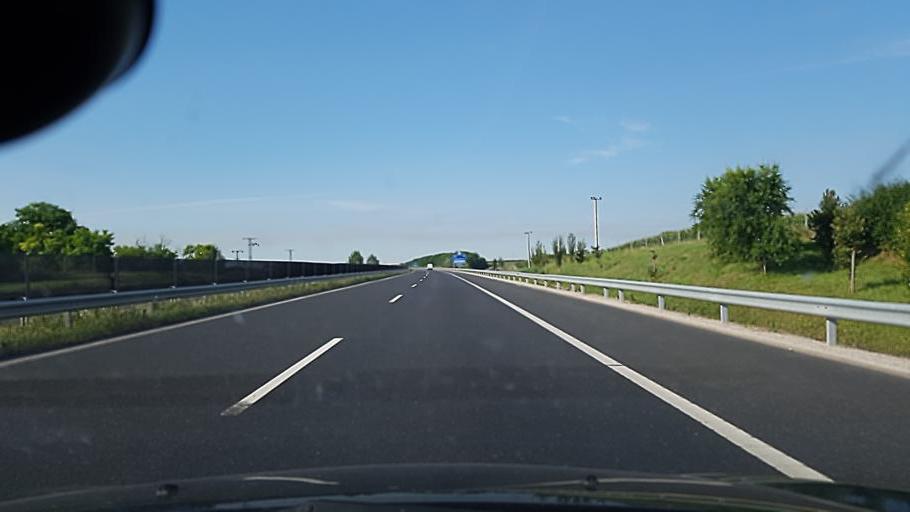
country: HU
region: Fejer
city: Racalmas
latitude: 47.0080
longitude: 18.8906
